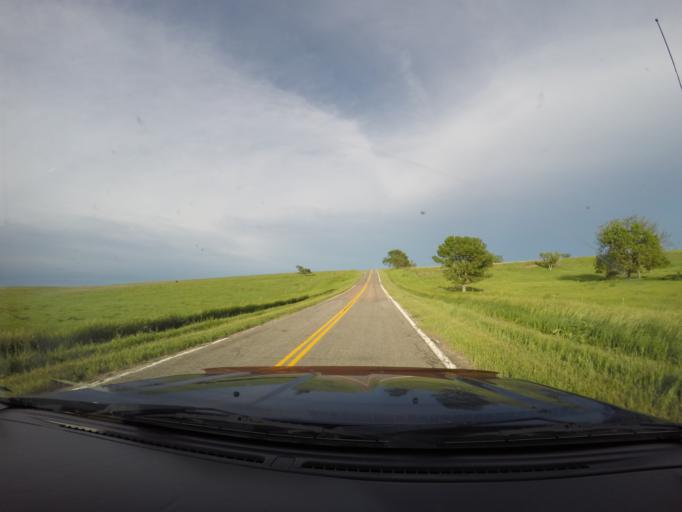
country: US
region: Kansas
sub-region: Smith County
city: Smith Center
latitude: 39.8281
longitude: -98.5757
